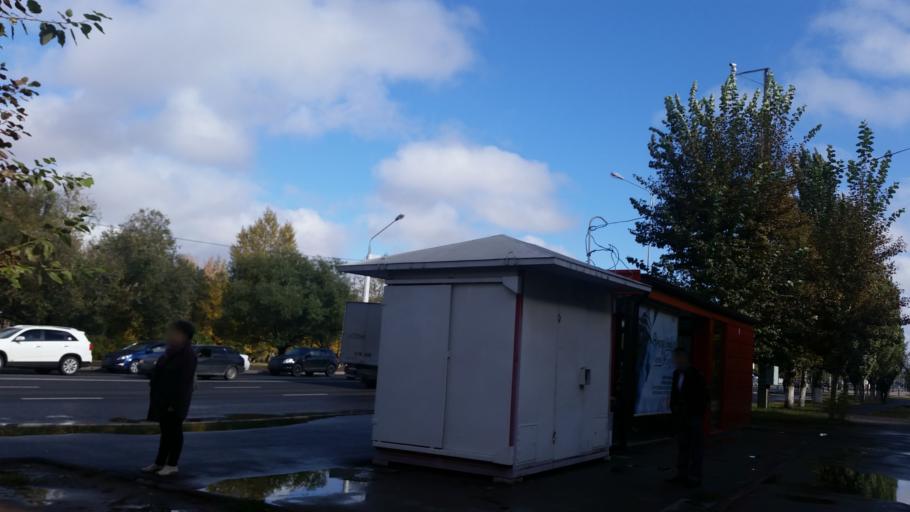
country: KZ
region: Astana Qalasy
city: Astana
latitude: 51.1584
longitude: 71.4753
